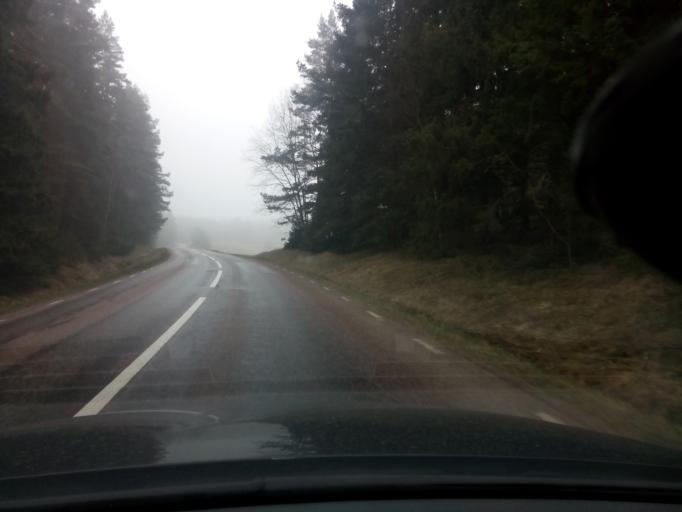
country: SE
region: Soedermanland
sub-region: Nykopings Kommun
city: Nykoping
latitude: 58.8536
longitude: 17.0593
